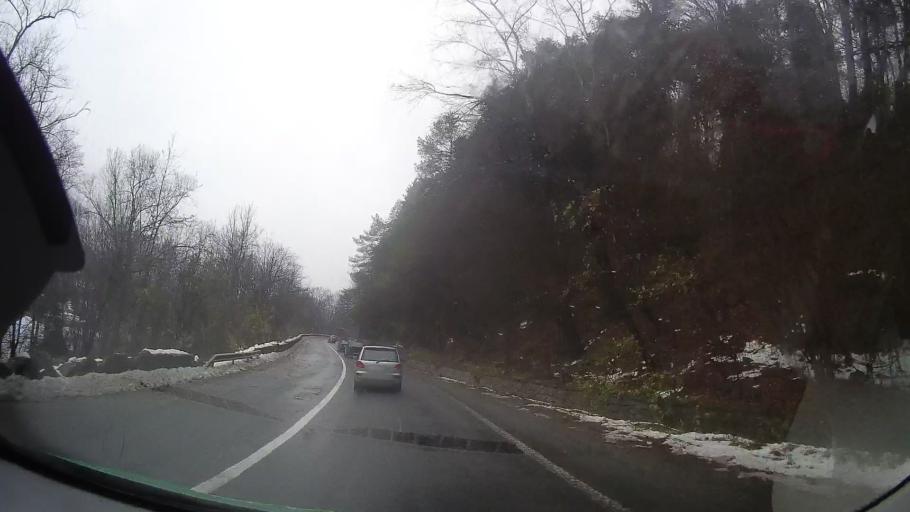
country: RO
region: Neamt
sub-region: Comuna Tarcau
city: Tarcau
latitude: 46.8978
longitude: 26.1213
